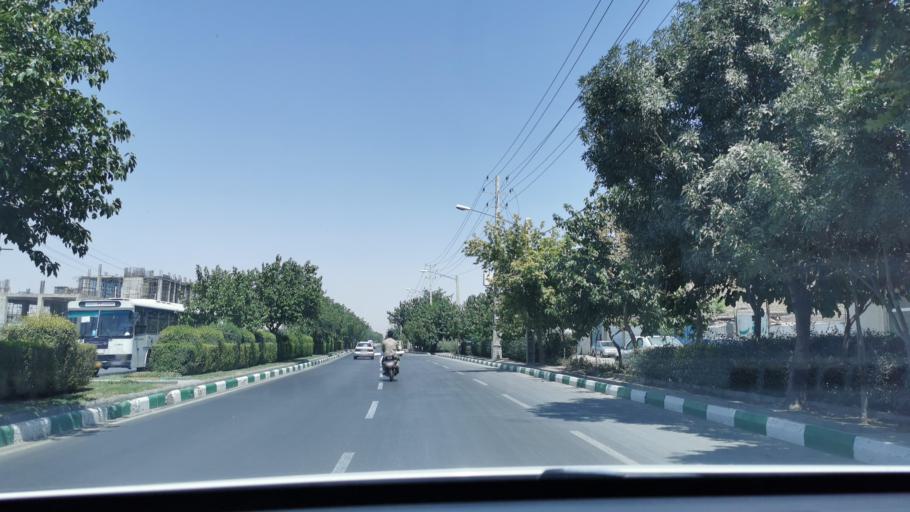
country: IR
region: Razavi Khorasan
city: Mashhad
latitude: 36.3517
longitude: 59.6303
